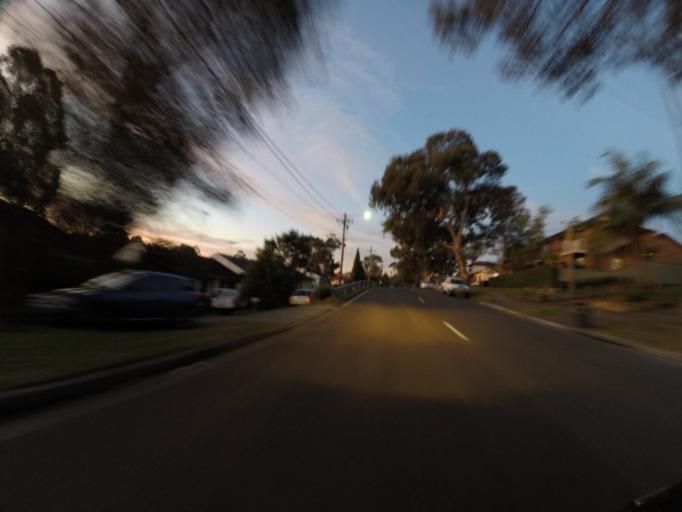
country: AU
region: New South Wales
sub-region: Sutherland Shire
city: Heathcote
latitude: -34.0891
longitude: 151.0034
